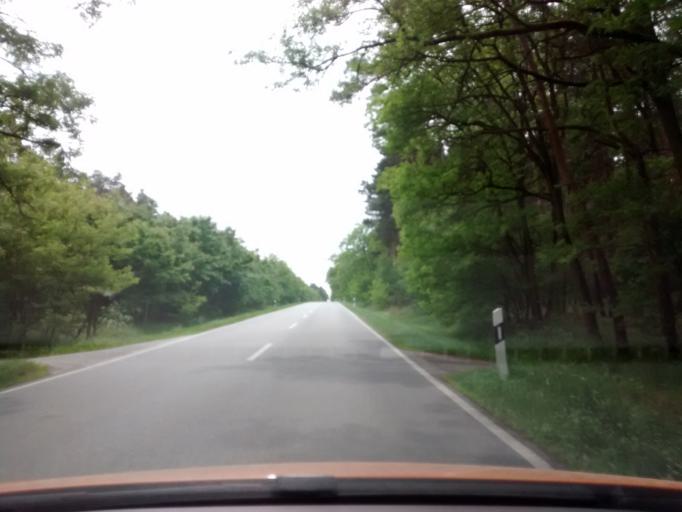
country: DE
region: Saxony-Anhalt
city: Holzdorf
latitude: 51.8830
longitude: 13.1427
